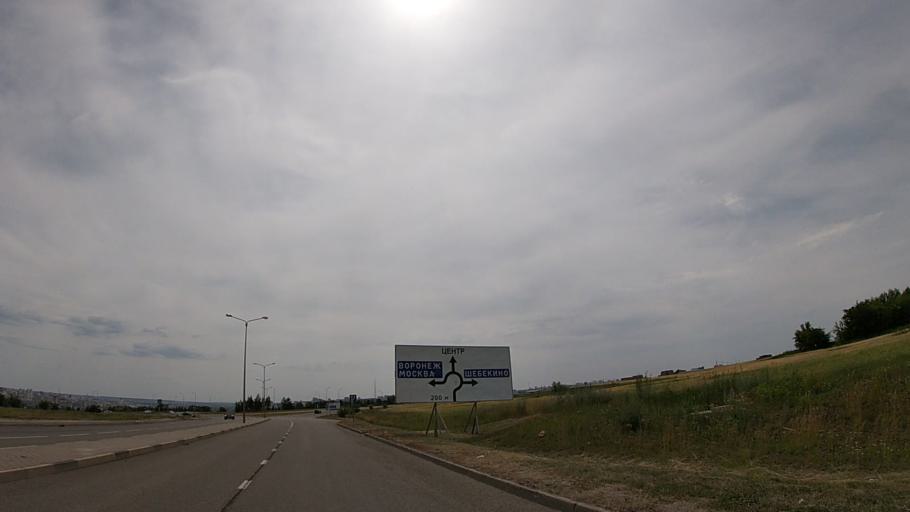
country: RU
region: Belgorod
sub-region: Belgorodskiy Rayon
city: Belgorod
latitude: 50.5940
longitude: 36.5272
